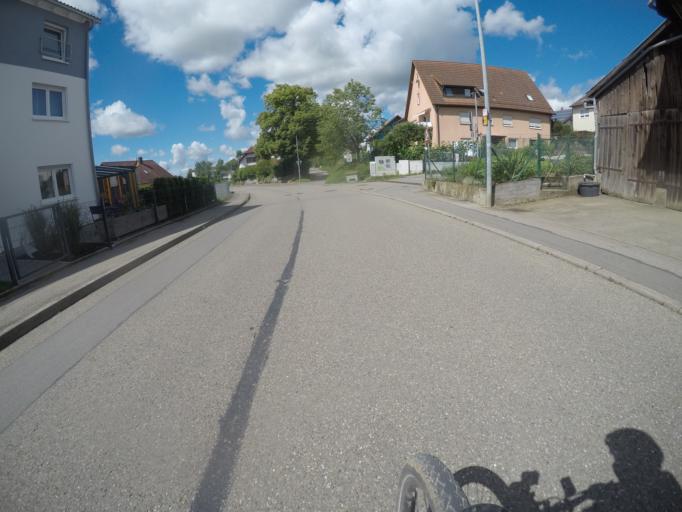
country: DE
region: Baden-Wuerttemberg
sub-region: Regierungsbezirk Stuttgart
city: Motzingen
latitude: 48.5318
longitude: 8.7724
